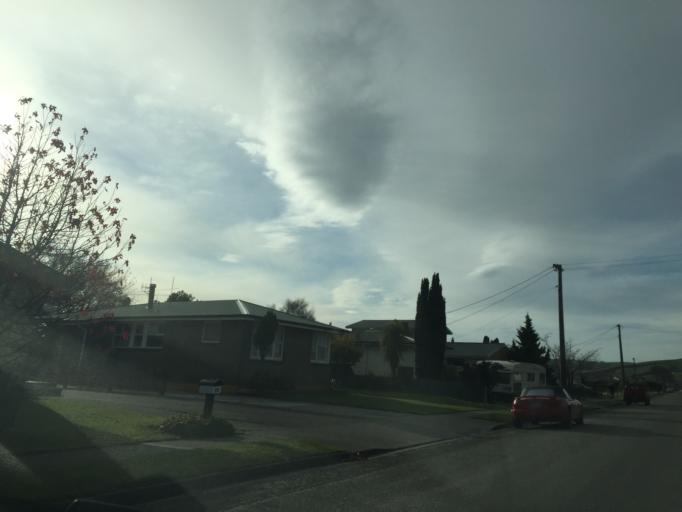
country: NZ
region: Southland
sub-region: Gore District
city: Gore
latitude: -46.1142
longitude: 168.9267
